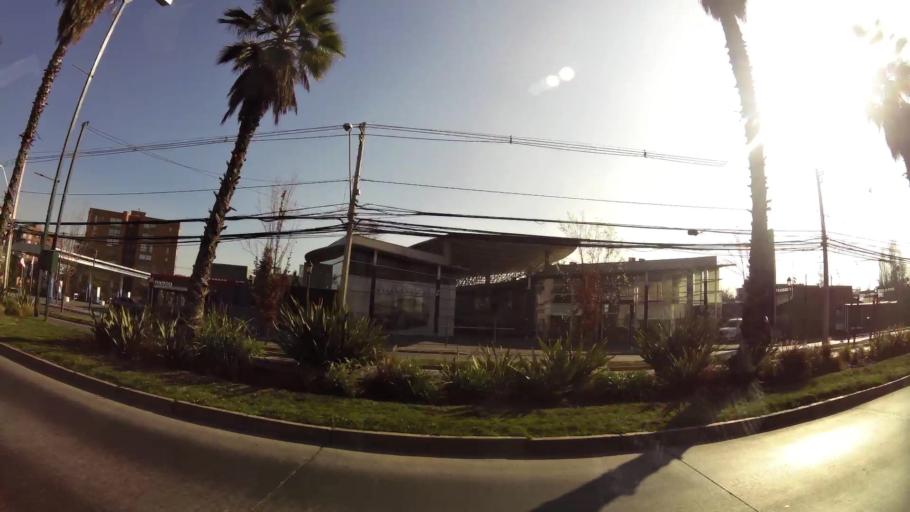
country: CL
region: Santiago Metropolitan
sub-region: Provincia de Santiago
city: Villa Presidente Frei, Nunoa, Santiago, Chile
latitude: -33.3596
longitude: -70.5168
